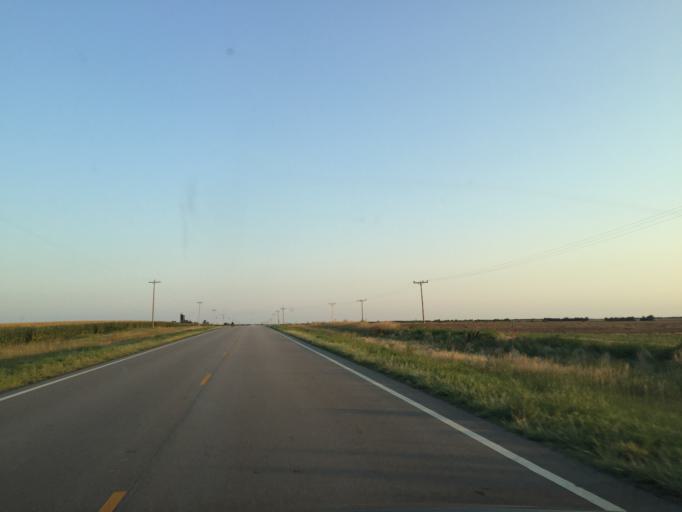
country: US
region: Kansas
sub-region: Ellsworth County
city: Ellsworth
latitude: 38.5540
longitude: -98.2017
